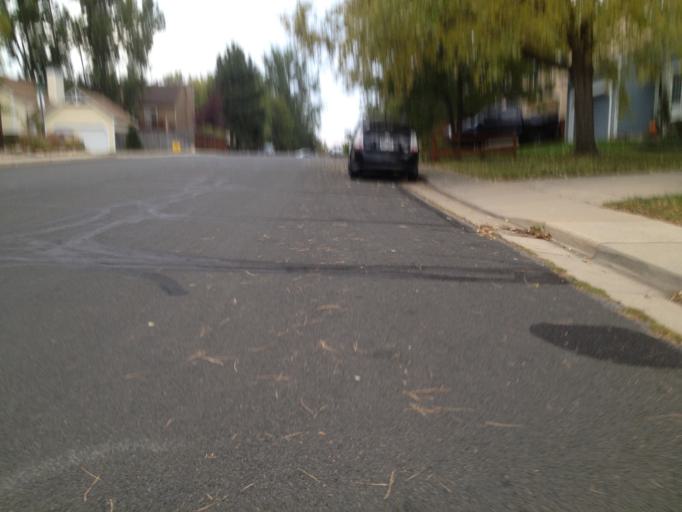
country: US
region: Colorado
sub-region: Boulder County
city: Louisville
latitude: 39.9899
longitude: -105.1438
